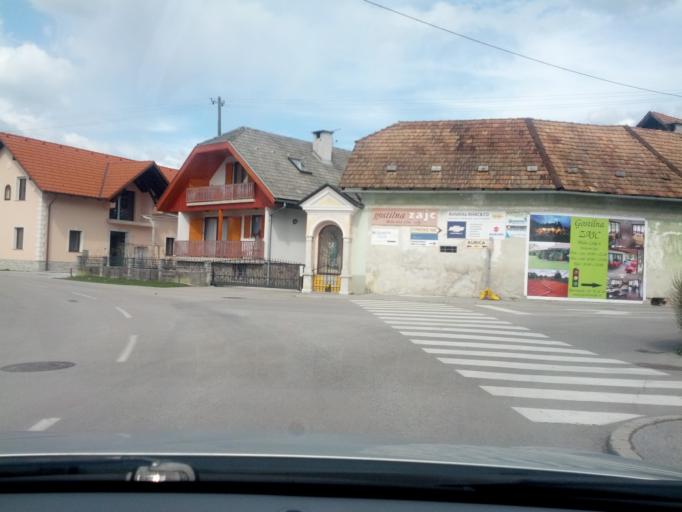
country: SI
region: Dol pri Ljubljani
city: Dol pri Ljubljani
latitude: 46.1065
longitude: 14.5944
